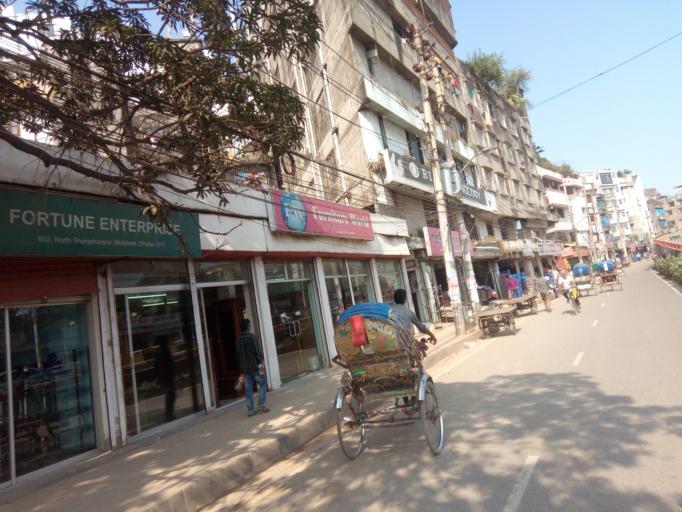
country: BD
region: Dhaka
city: Paltan
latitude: 23.7428
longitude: 90.4220
